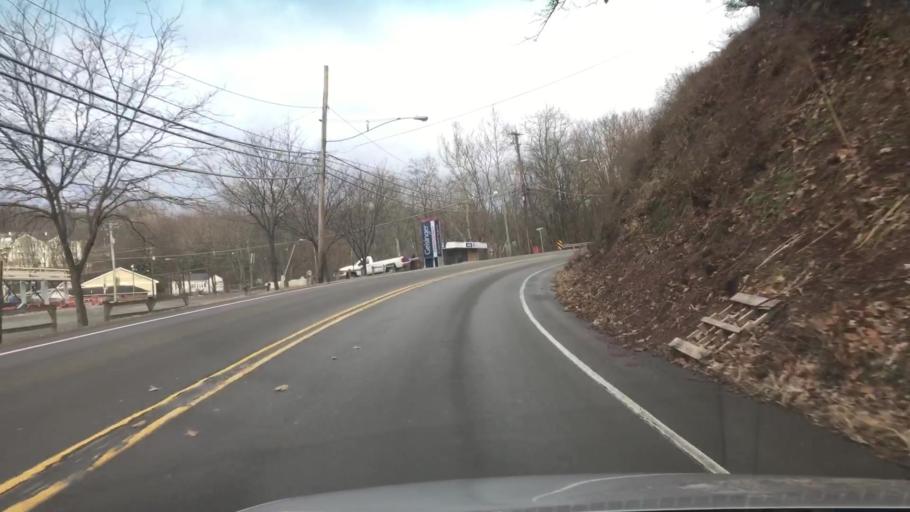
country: US
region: Pennsylvania
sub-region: Columbia County
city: Bloomsburg
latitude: 41.0069
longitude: -76.4500
